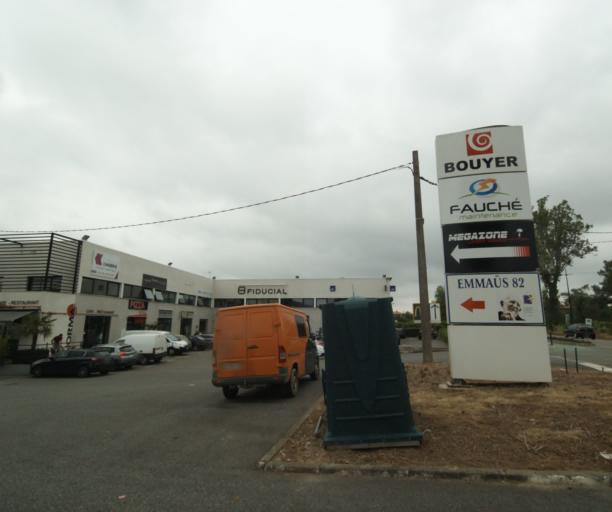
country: FR
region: Midi-Pyrenees
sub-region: Departement du Tarn-et-Garonne
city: Montauban
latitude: 43.9956
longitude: 1.3379
